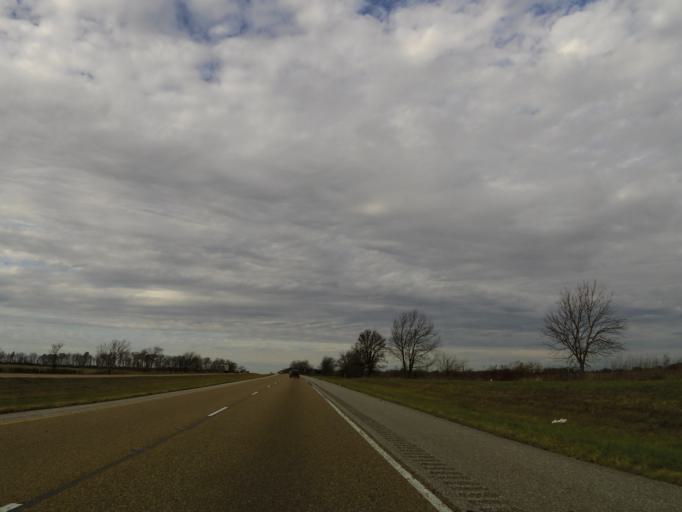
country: US
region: Illinois
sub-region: Clinton County
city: Wamac
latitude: 38.3895
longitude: -89.2218
